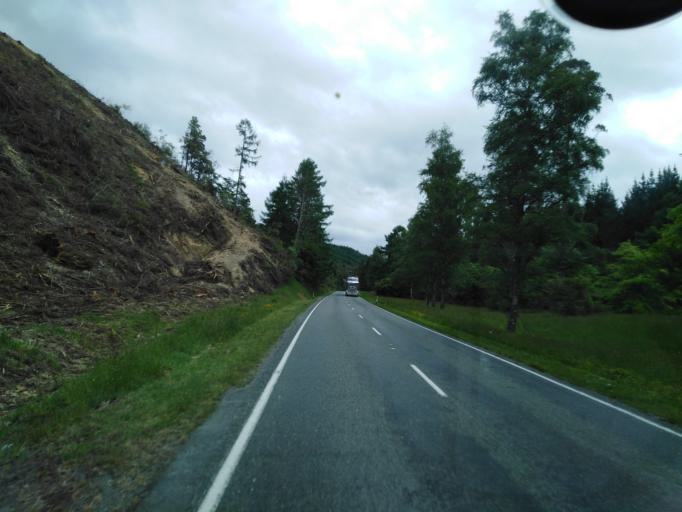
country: NZ
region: Tasman
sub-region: Tasman District
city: Wakefield
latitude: -41.6037
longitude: 172.7590
